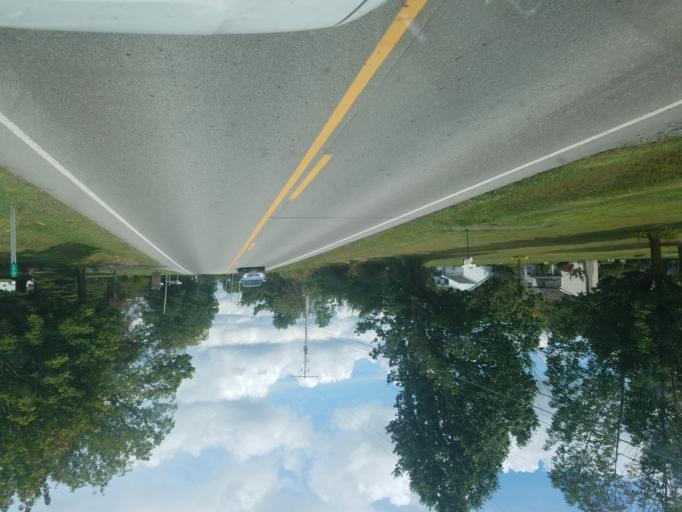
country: US
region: Ohio
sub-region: Geauga County
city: Middlefield
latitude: 41.4179
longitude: -81.0382
